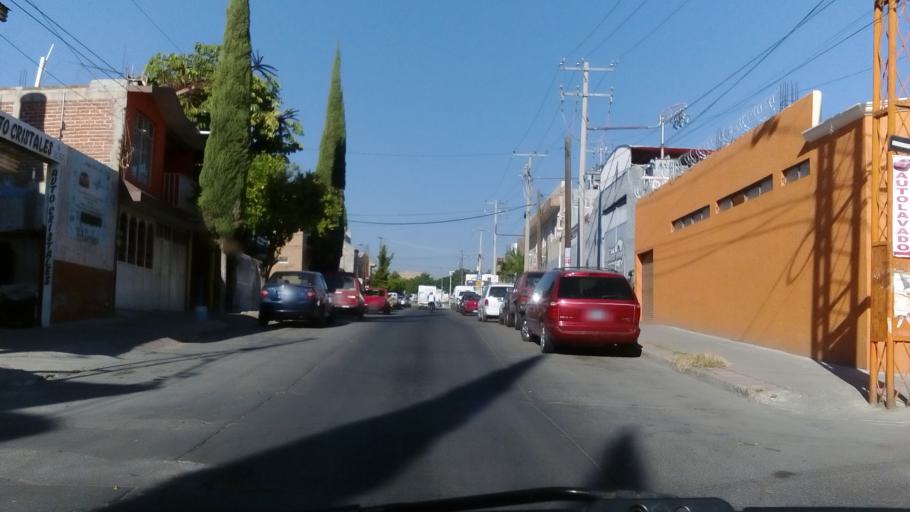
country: MX
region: Guanajuato
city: Leon
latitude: 21.1158
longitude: -101.7065
